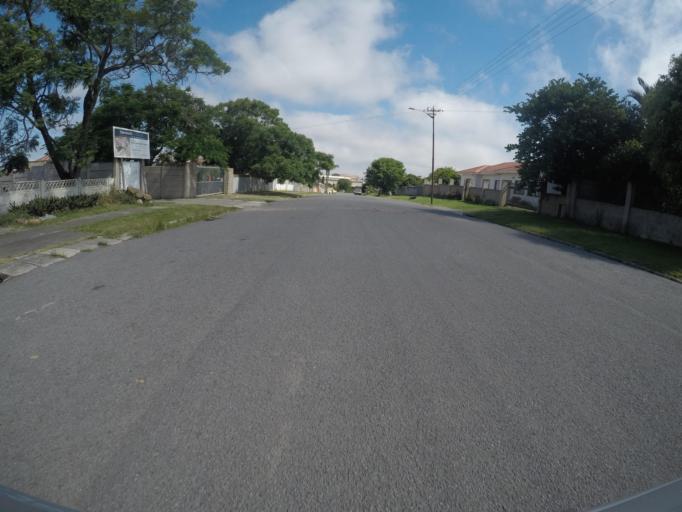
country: ZA
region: Eastern Cape
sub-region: Buffalo City Metropolitan Municipality
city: East London
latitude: -32.9790
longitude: 27.8906
